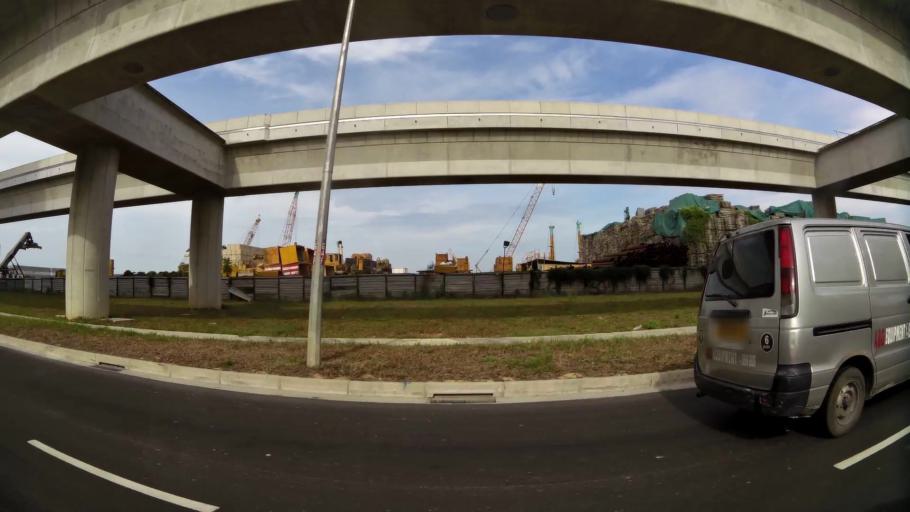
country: MY
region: Johor
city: Johor Bahru
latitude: 1.3364
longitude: 103.6355
